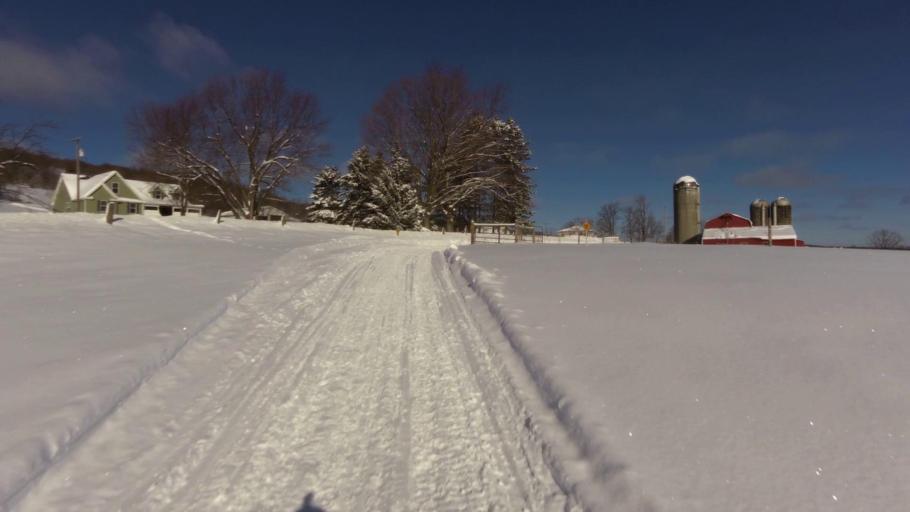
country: US
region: New York
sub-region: Chautauqua County
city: Falconer
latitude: 42.2722
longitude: -79.1145
